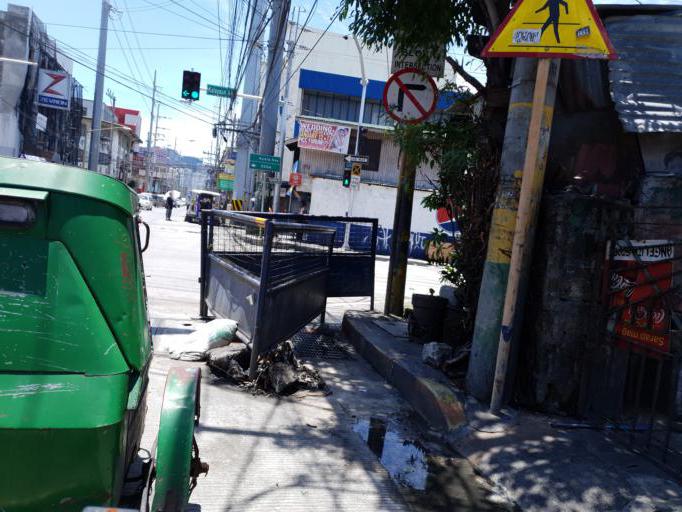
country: PH
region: Metro Manila
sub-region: Makati City
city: Makati City
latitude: 14.5709
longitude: 121.0151
